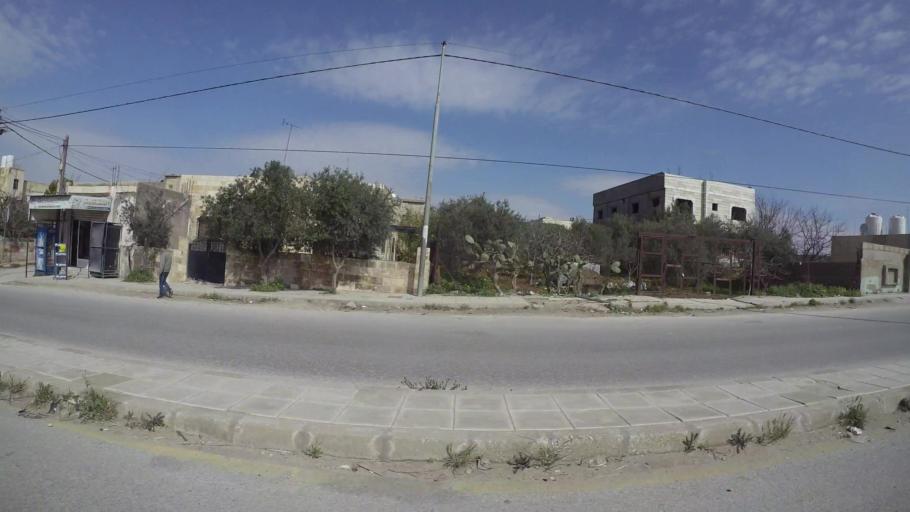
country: JO
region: Amman
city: Al Jubayhah
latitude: 32.0808
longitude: 35.8428
